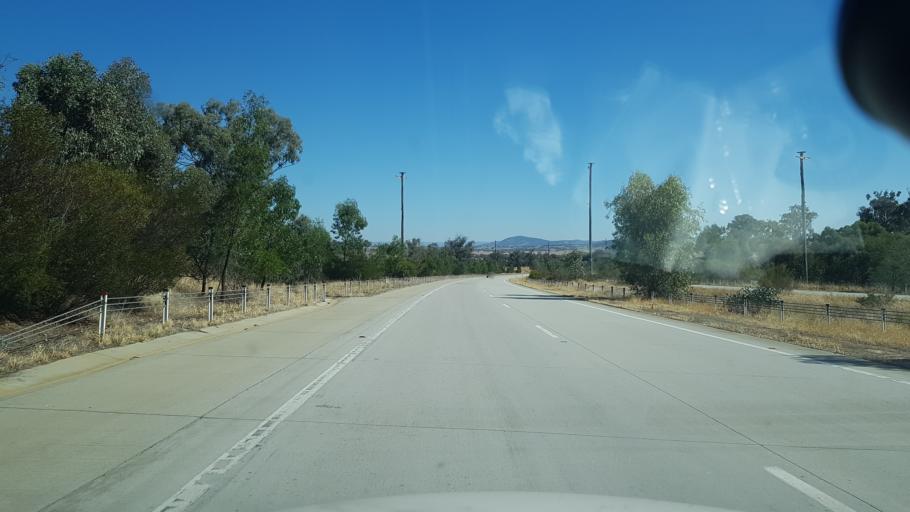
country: AU
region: New South Wales
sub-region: Albury Municipality
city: Lavington
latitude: -35.9225
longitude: 147.0931
